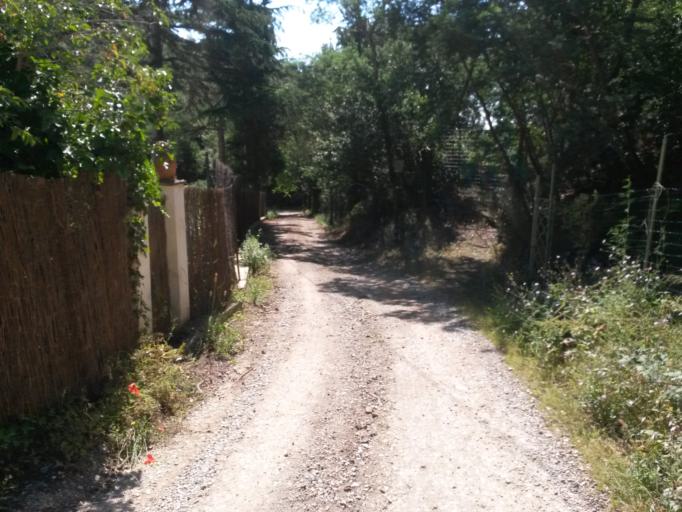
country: IT
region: Tuscany
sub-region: Provincia di Livorno
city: Porto Azzurro
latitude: 42.7819
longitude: 10.3942
